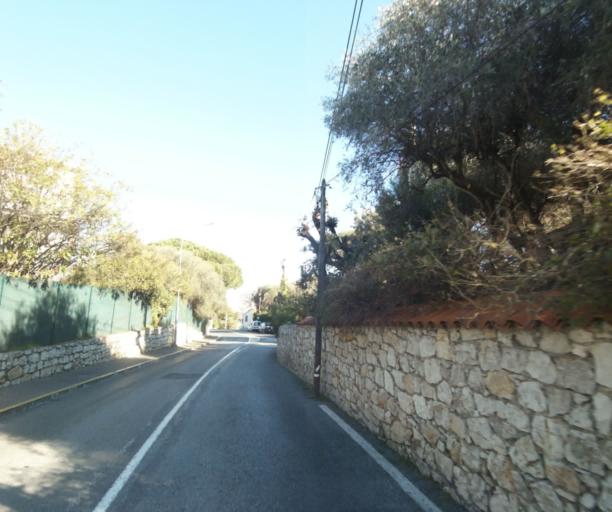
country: FR
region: Provence-Alpes-Cote d'Azur
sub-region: Departement des Alpes-Maritimes
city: Antibes
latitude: 43.5734
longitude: 7.1194
